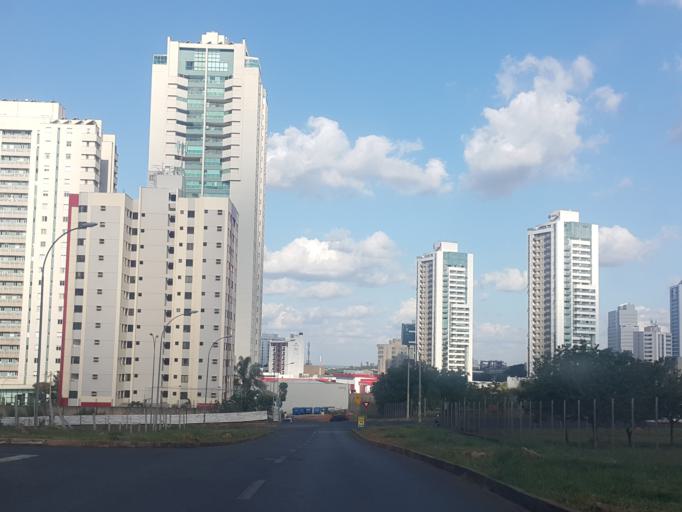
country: BR
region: Federal District
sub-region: Brasilia
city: Brasilia
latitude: -15.8409
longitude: -48.0362
